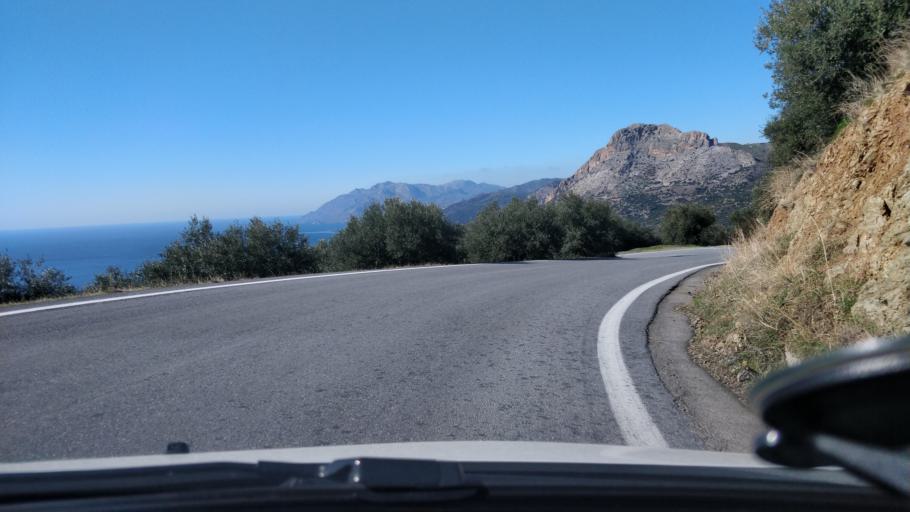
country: GR
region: Crete
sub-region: Nomos Irakleiou
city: Arkalochori
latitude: 35.0066
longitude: 25.4408
